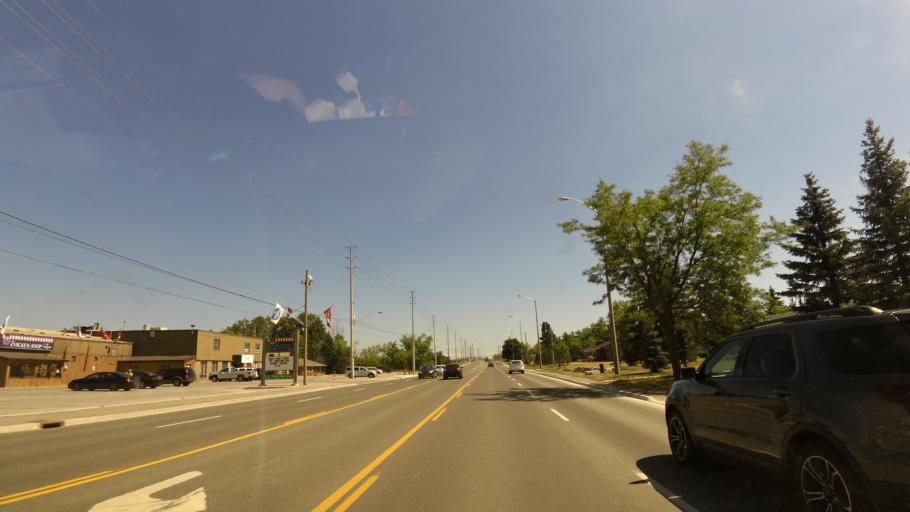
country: CA
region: Ontario
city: Brampton
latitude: 43.6113
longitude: -79.8030
